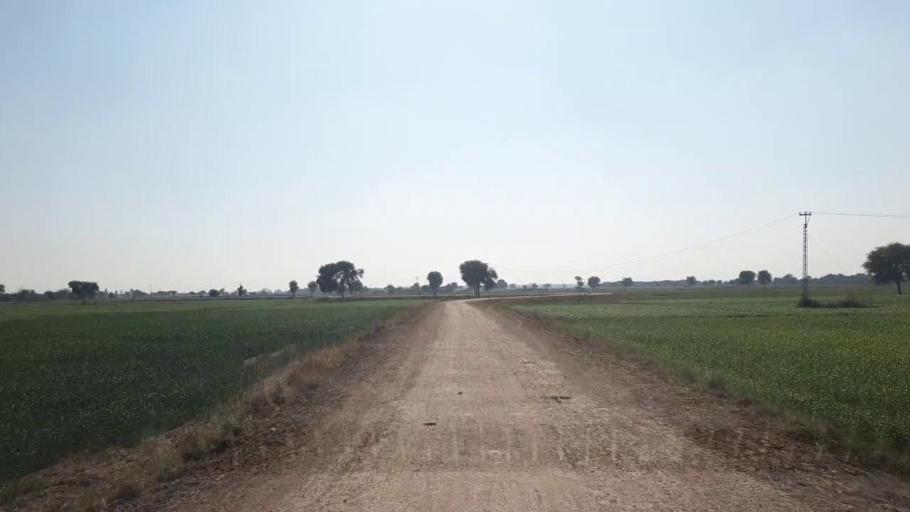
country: PK
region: Sindh
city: Shahdadpur
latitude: 25.9540
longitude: 68.6559
